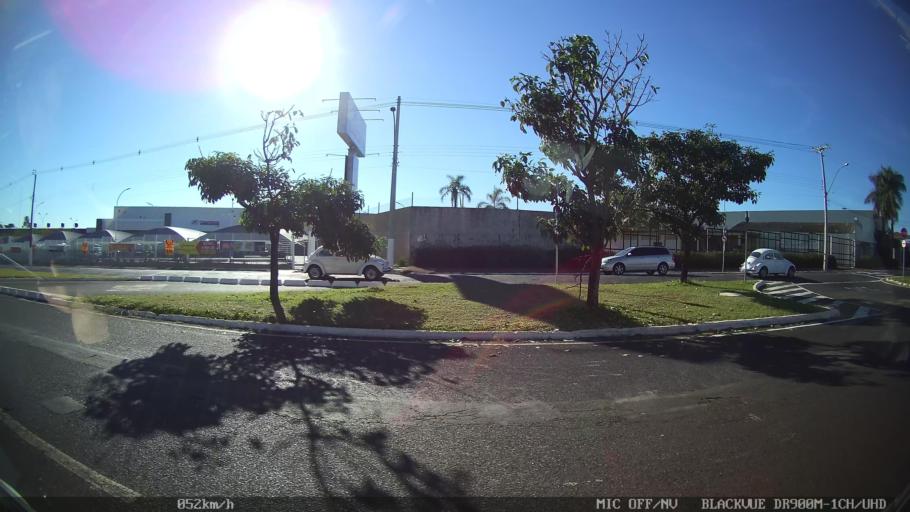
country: BR
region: Sao Paulo
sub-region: Franca
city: Franca
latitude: -20.5687
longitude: -47.3933
